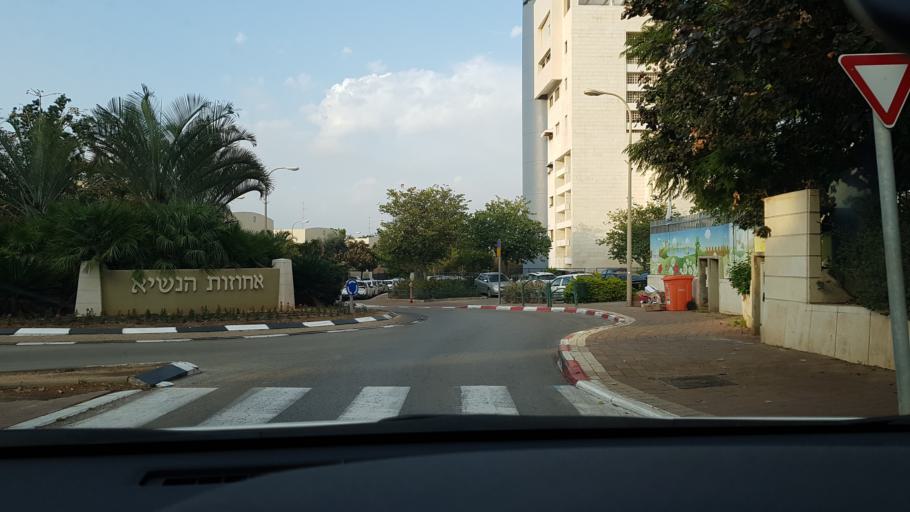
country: IL
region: Central District
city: Ness Ziona
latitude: 31.9063
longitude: 34.8206
